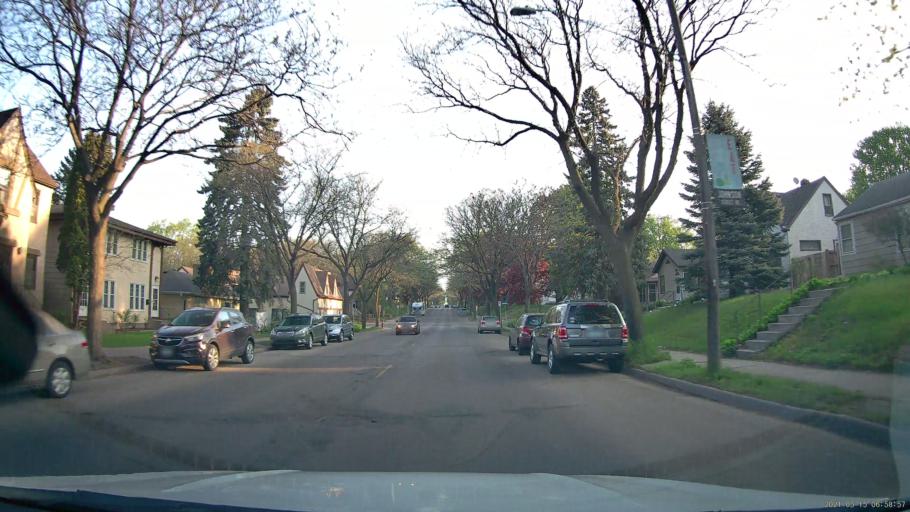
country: US
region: Minnesota
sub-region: Hennepin County
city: Saint Anthony
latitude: 45.0215
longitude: -93.2371
